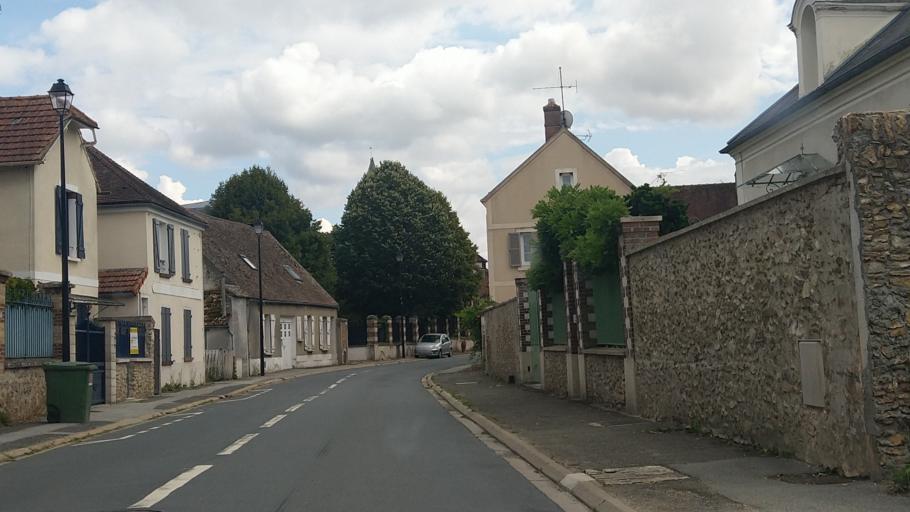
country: FR
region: Ile-de-France
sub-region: Departement des Yvelines
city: Sonchamp
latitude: 48.5778
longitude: 1.8755
